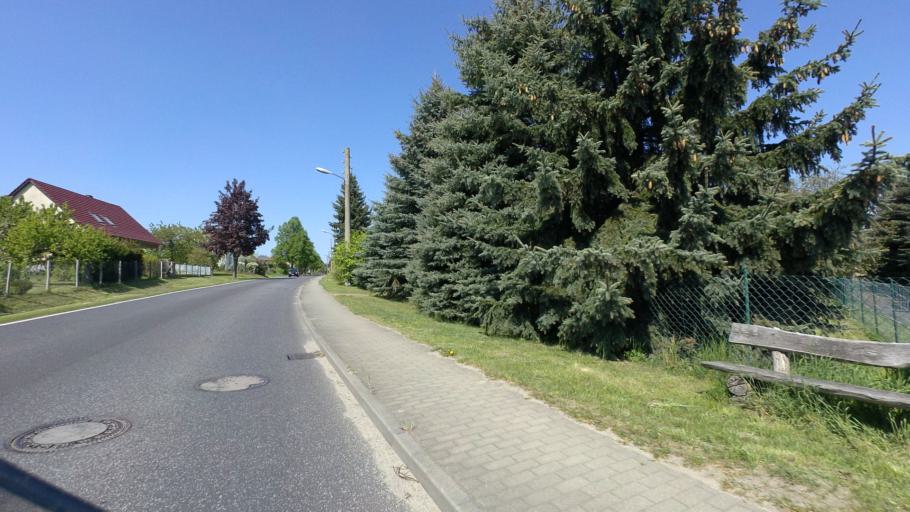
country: DE
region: Brandenburg
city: Friedland
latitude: 52.1079
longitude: 14.2584
